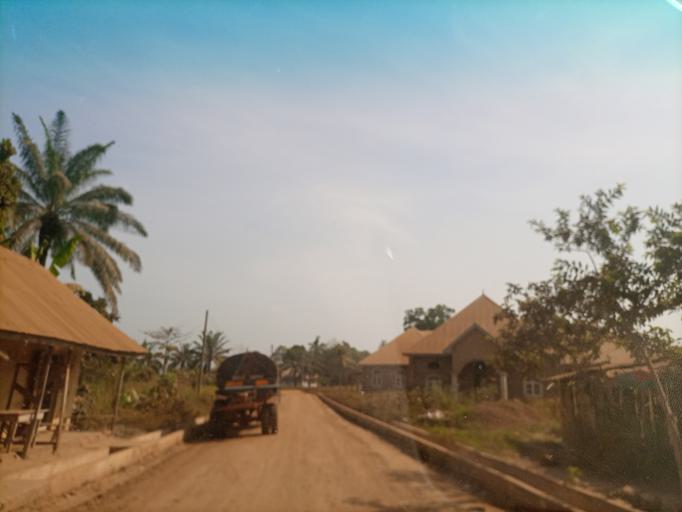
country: NG
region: Enugu
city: Eha Amufu
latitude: 6.6625
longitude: 7.7570
